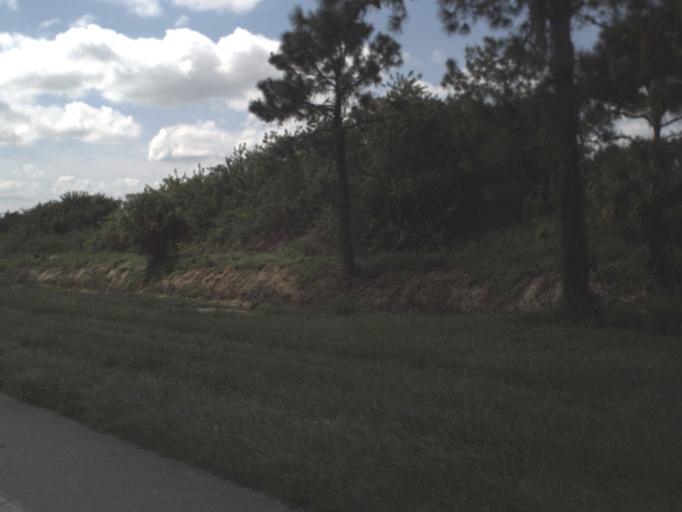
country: US
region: Florida
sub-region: Hendry County
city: LaBelle
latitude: 26.6876
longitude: -81.4368
